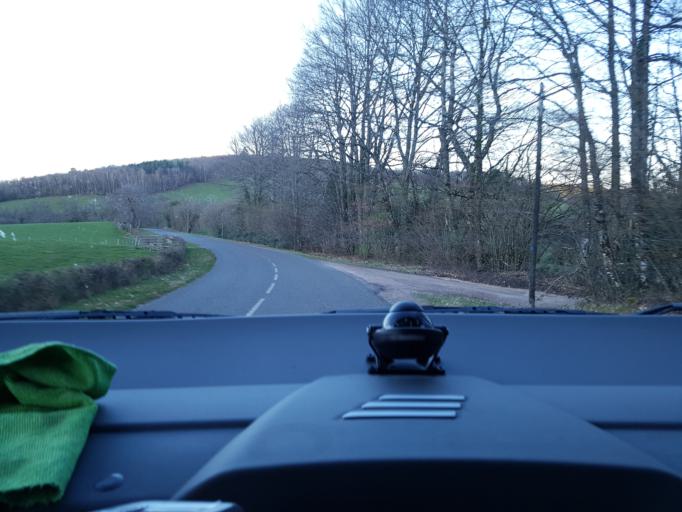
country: FR
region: Bourgogne
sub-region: Departement de Saone-et-Loire
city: Etang-sur-Arroux
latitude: 46.9201
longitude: 4.0743
